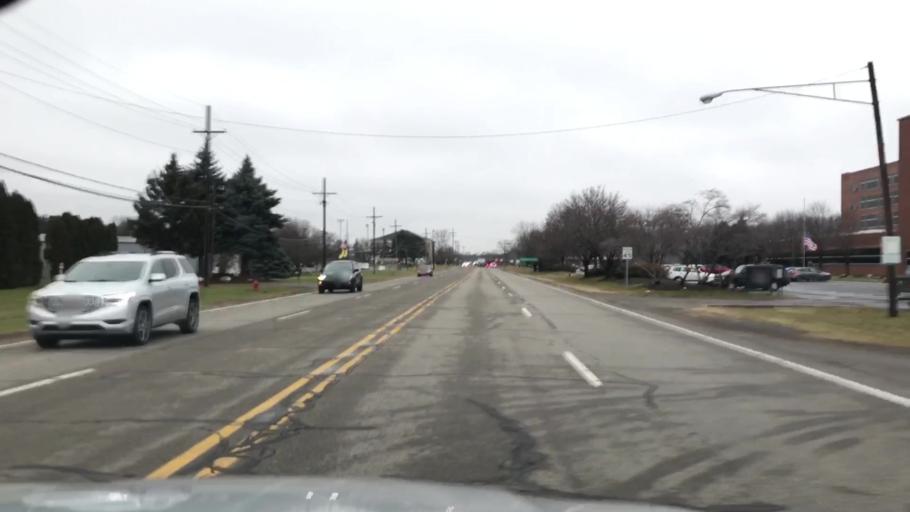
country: US
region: Michigan
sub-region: Wayne County
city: Plymouth
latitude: 42.3747
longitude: -83.4458
